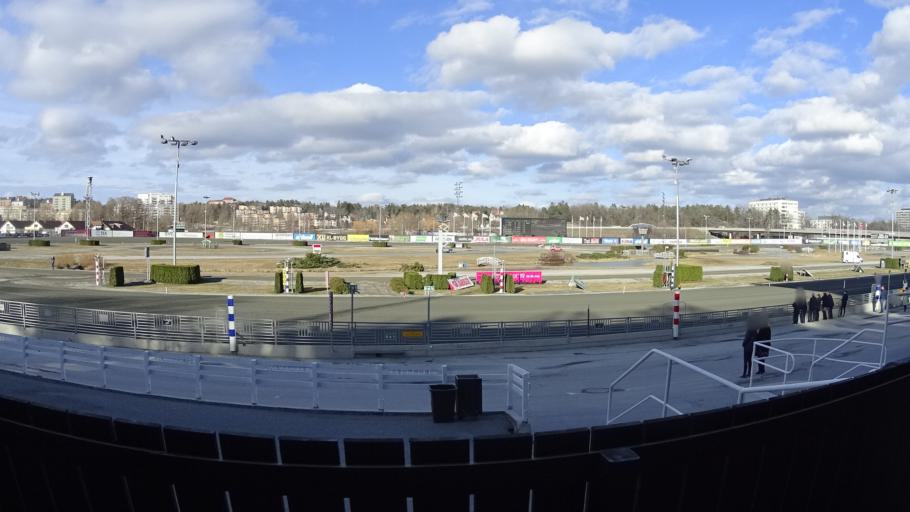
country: SE
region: Stockholm
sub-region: Stockholms Kommun
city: Bromma
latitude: 59.3669
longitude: 17.9378
